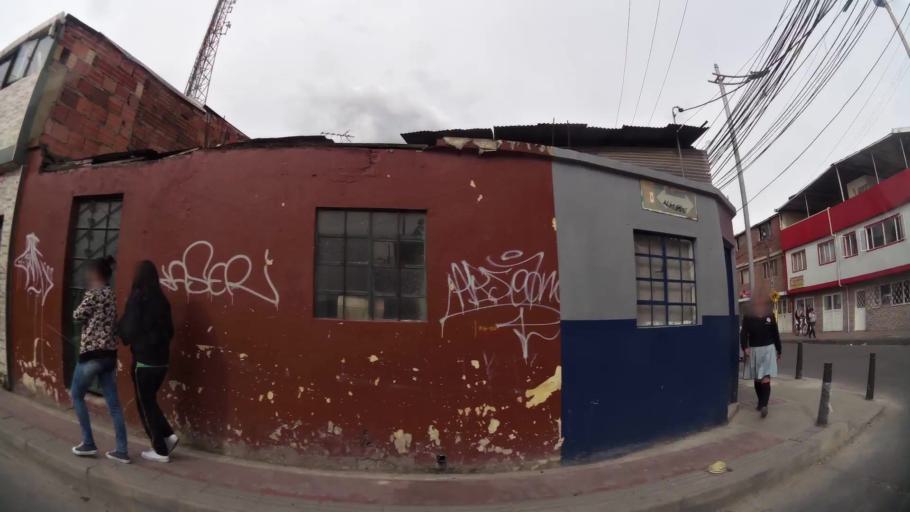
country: CO
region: Cundinamarca
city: Funza
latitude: 4.7074
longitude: -74.2120
